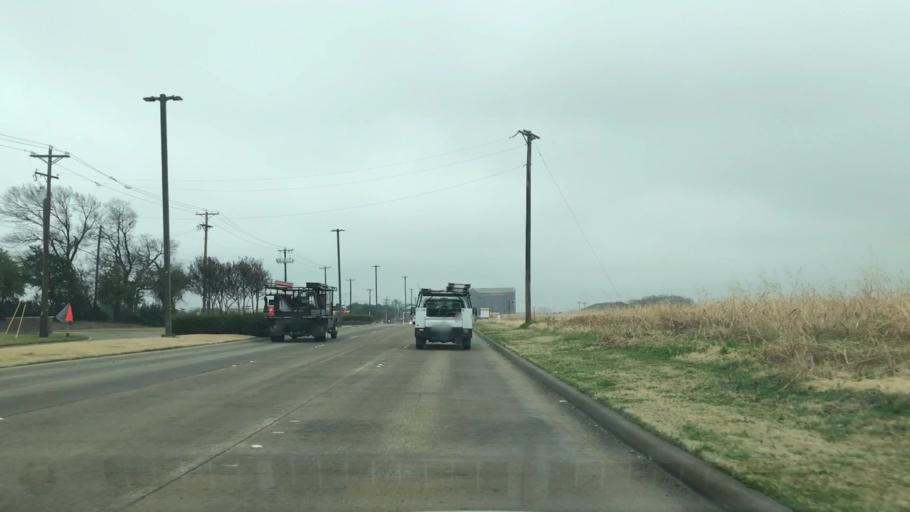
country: US
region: Texas
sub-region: Dallas County
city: Farmers Branch
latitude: 32.9180
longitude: -96.9304
